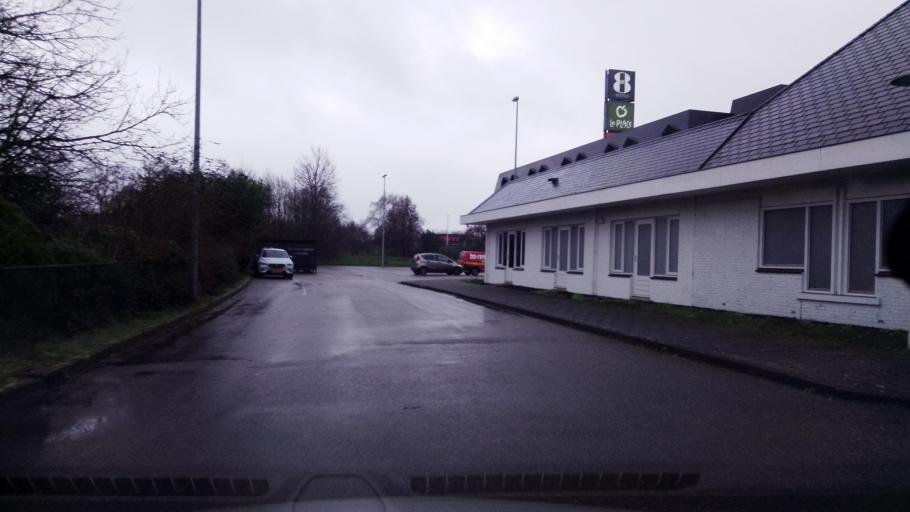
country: NL
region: Limburg
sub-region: Gemeente Peel en Maas
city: Maasbree
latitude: 51.3794
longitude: 5.9855
